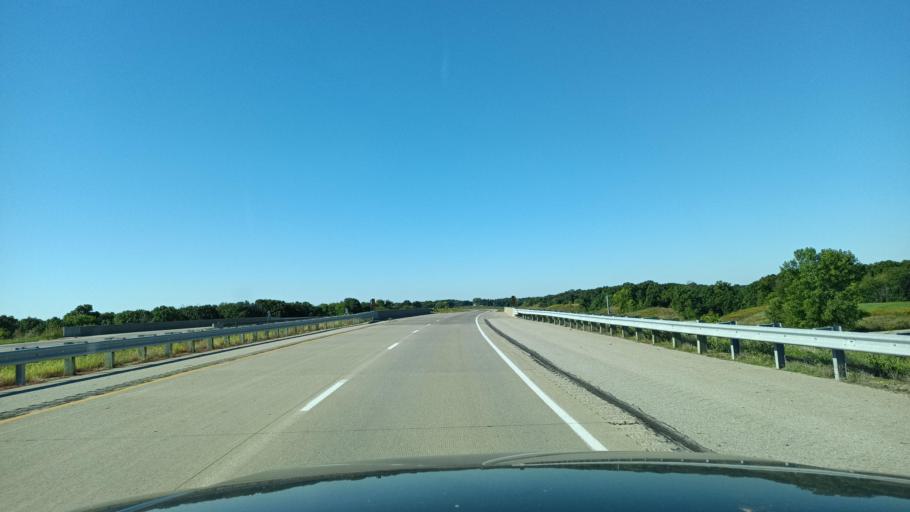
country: US
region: Iowa
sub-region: Lee County
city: Fort Madison
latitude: 40.6511
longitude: -91.3648
